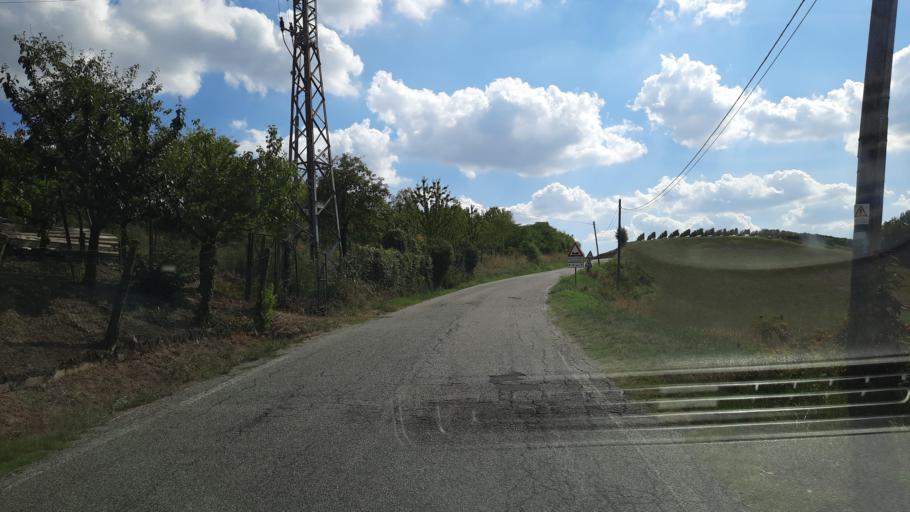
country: IT
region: Piedmont
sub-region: Provincia di Alessandria
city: Cereseto
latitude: 45.0840
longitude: 8.3166
